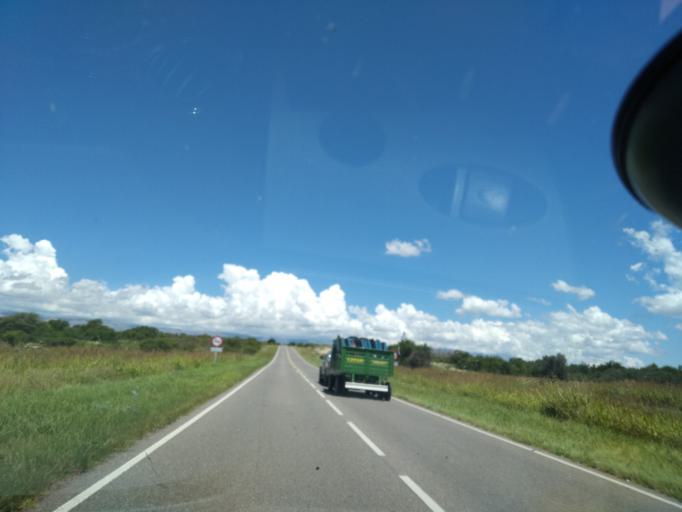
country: AR
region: Cordoba
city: Villa Cura Brochero
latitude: -31.6825
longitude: -65.0809
